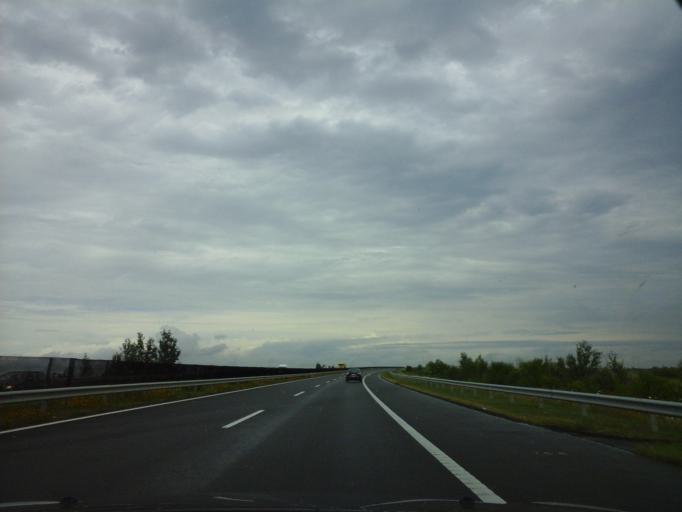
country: HU
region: Hajdu-Bihar
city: Polgar
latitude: 47.8163
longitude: 21.1547
